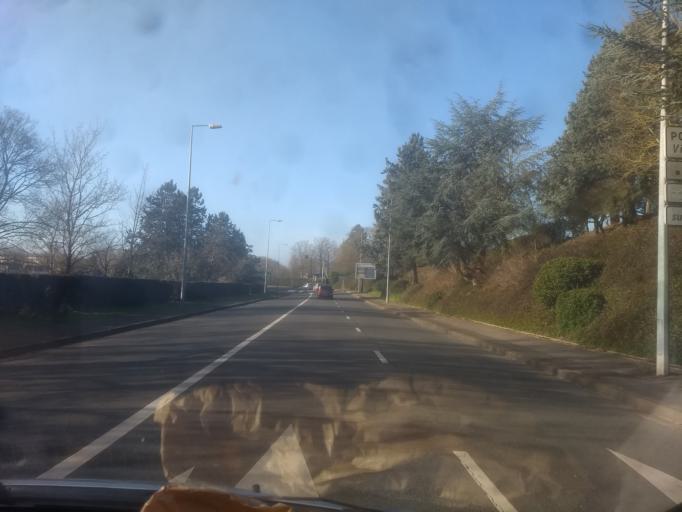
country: FR
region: Centre
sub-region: Departement du Cher
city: Bourges
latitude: 47.0952
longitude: 2.4026
